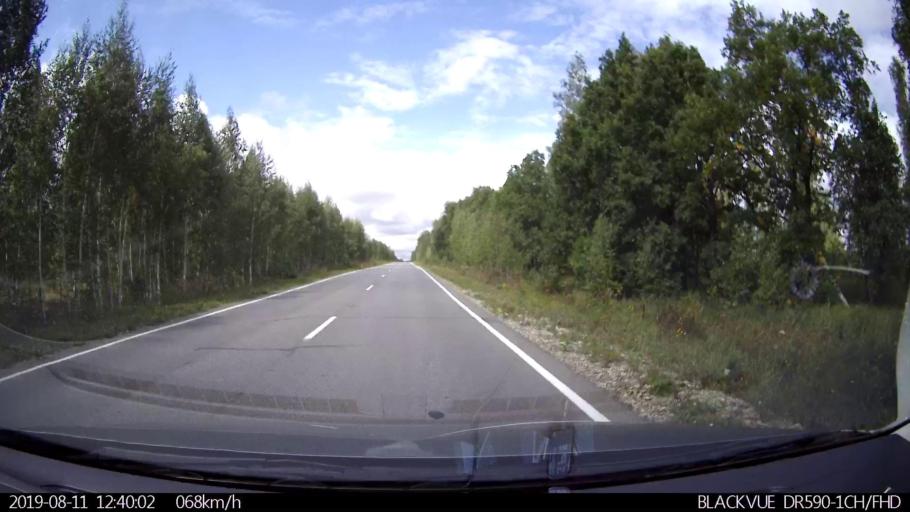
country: RU
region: Ulyanovsk
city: Ignatovka
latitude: 53.8364
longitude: 47.7868
